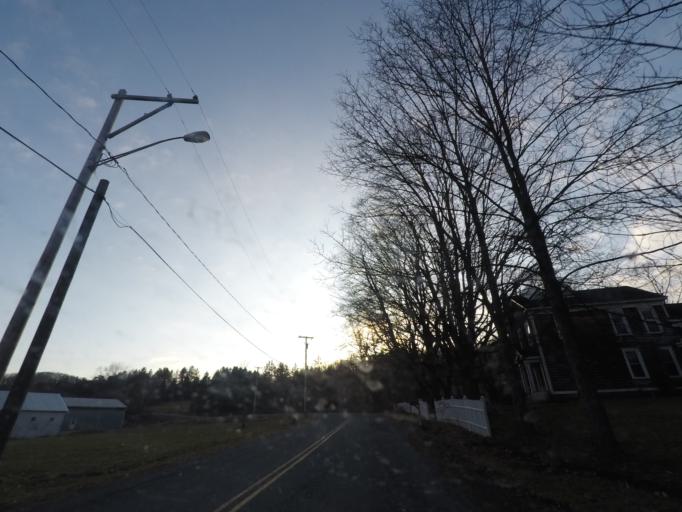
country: US
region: New York
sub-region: Rensselaer County
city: Wynantskill
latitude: 42.7053
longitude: -73.6343
